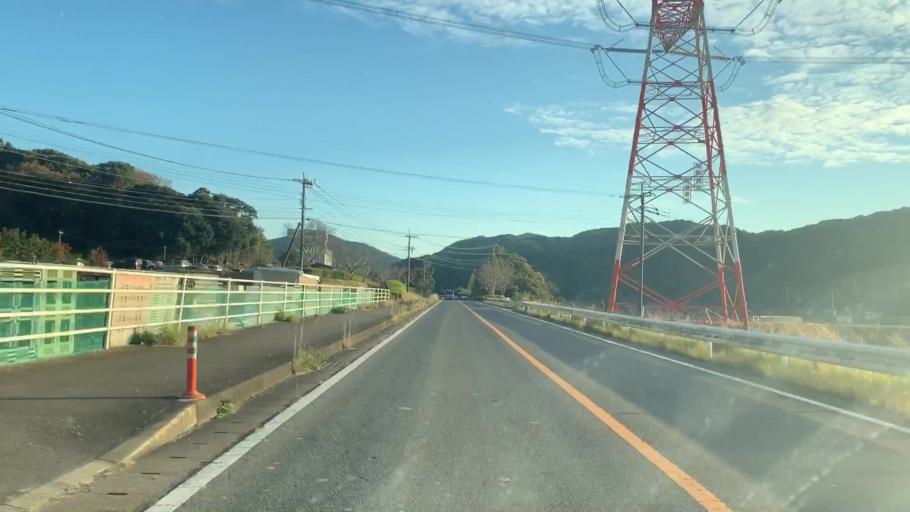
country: JP
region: Saga Prefecture
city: Karatsu
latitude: 33.3863
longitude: 129.9882
